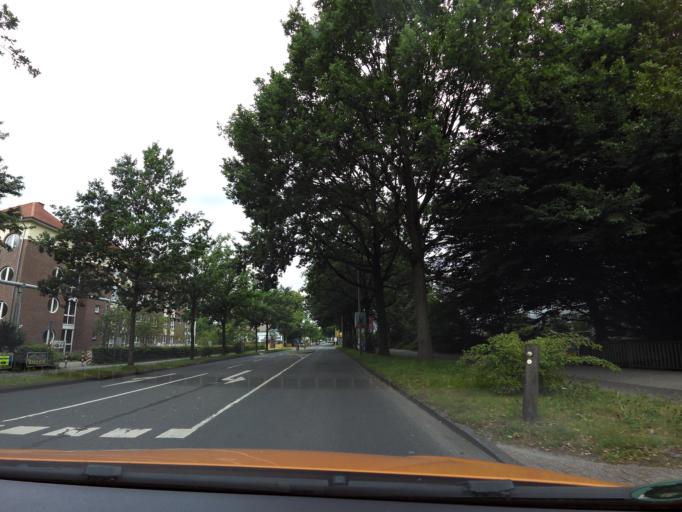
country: DE
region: Lower Saxony
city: Oldenburg
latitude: 53.1492
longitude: 8.1808
